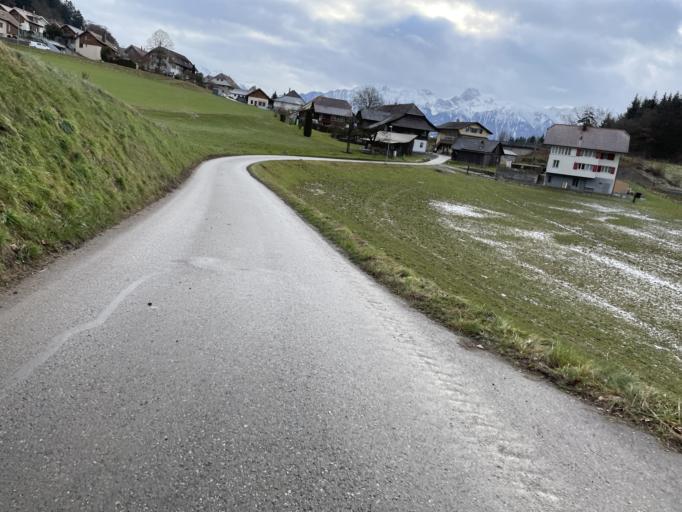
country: CH
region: Bern
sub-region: Thun District
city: Heimberg
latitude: 46.8030
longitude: 7.6048
